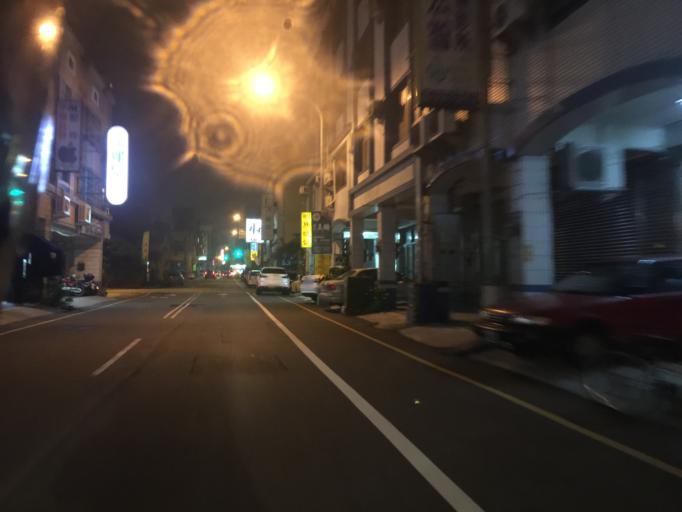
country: TW
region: Taiwan
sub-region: Miaoli
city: Miaoli
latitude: 24.5654
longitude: 120.8233
